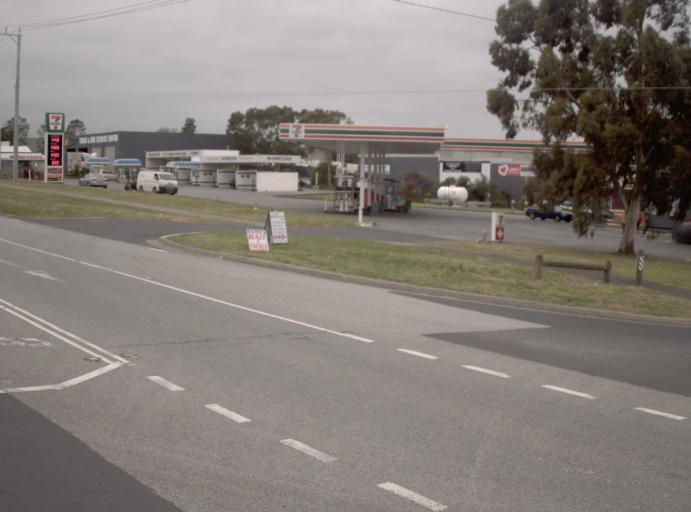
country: AU
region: Victoria
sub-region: Casey
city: Hallam
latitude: -38.0117
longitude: 145.2722
